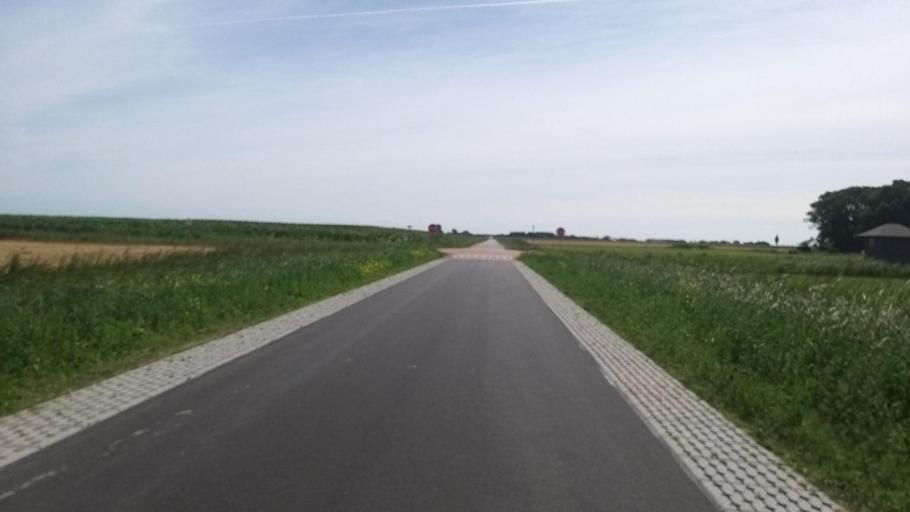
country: NL
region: North Holland
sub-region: Gemeente Texel
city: Den Burg
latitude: 53.1059
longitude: 4.8347
